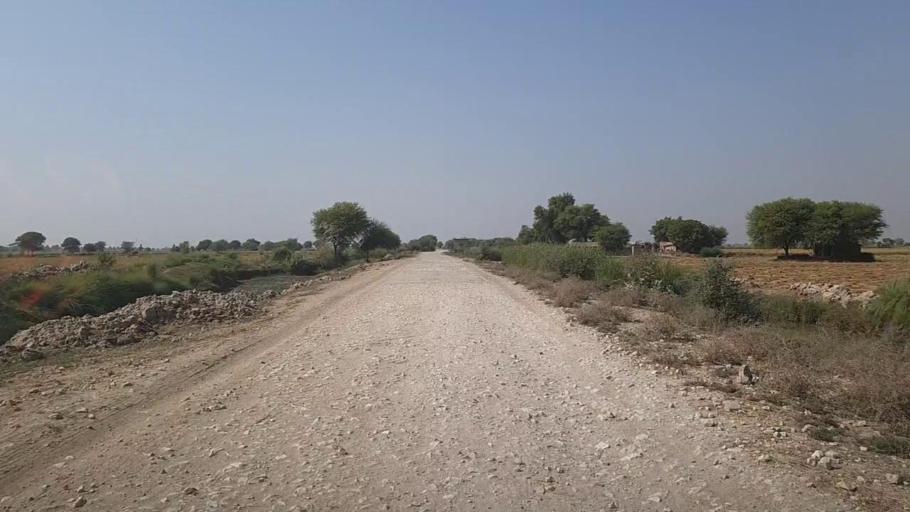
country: PK
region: Sindh
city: Kandhkot
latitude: 28.3926
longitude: 69.2811
